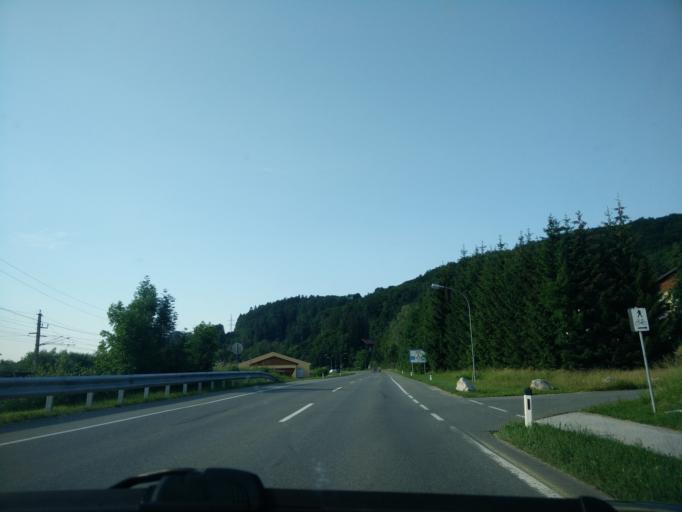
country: AT
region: Salzburg
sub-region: Politischer Bezirk Salzburg-Umgebung
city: Elsbethen
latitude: 47.7344
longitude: 13.0887
